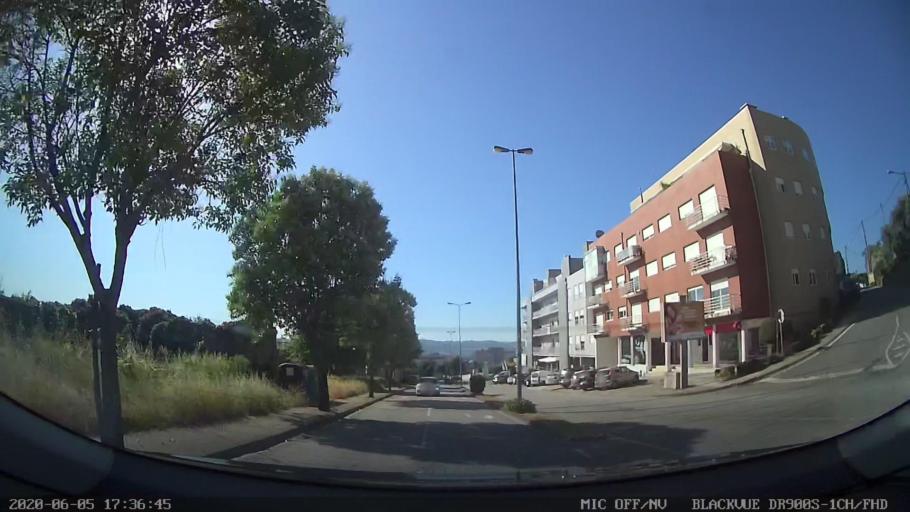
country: PT
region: Porto
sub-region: Penafiel
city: Penafiel
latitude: 41.2110
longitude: -8.2819
